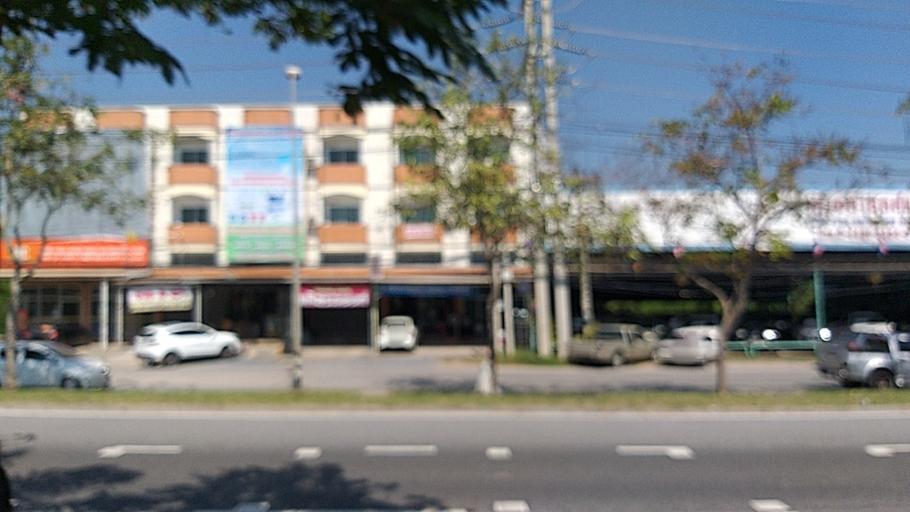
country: TH
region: Nakhon Ratchasima
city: Nakhon Ratchasima
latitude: 14.9571
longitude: 102.0378
